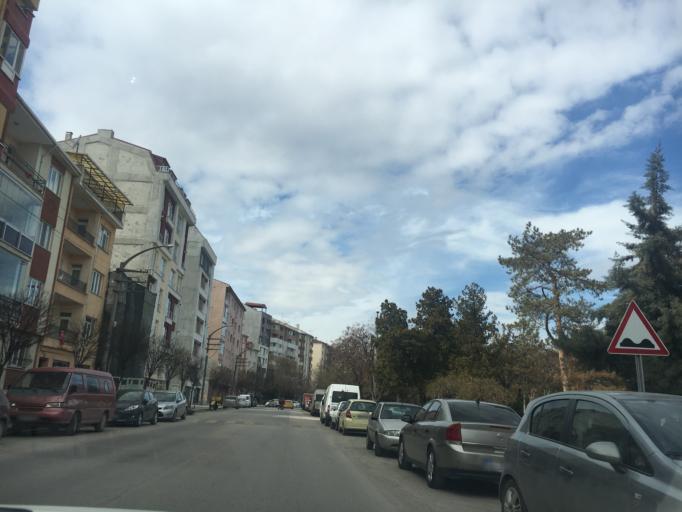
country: TR
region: Eskisehir
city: Eskisehir
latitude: 39.7805
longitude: 30.5292
